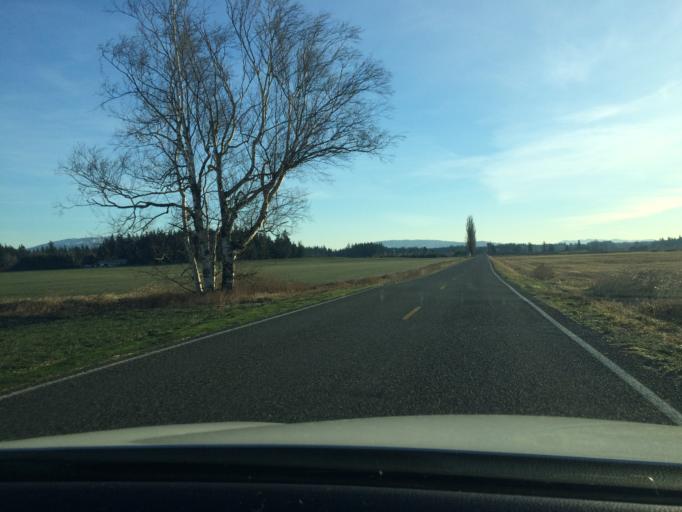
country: US
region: Washington
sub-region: Whatcom County
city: Everson
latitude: 48.9066
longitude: -122.3974
